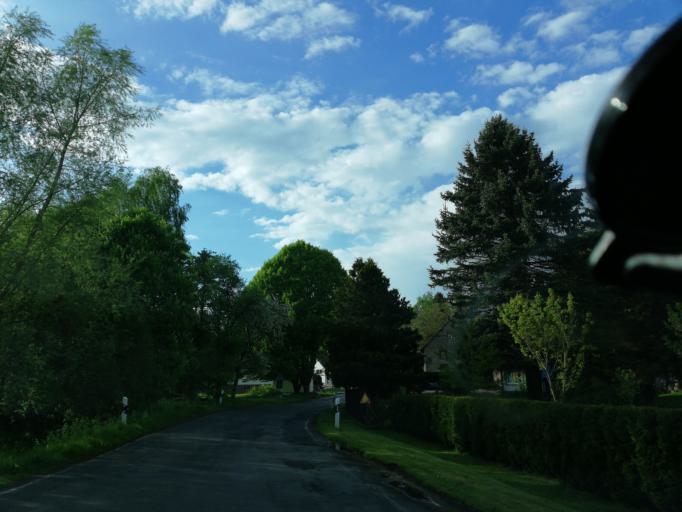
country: DE
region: North Rhine-Westphalia
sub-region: Regierungsbezirk Detmold
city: Dorentrup
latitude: 52.1249
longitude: 8.9991
